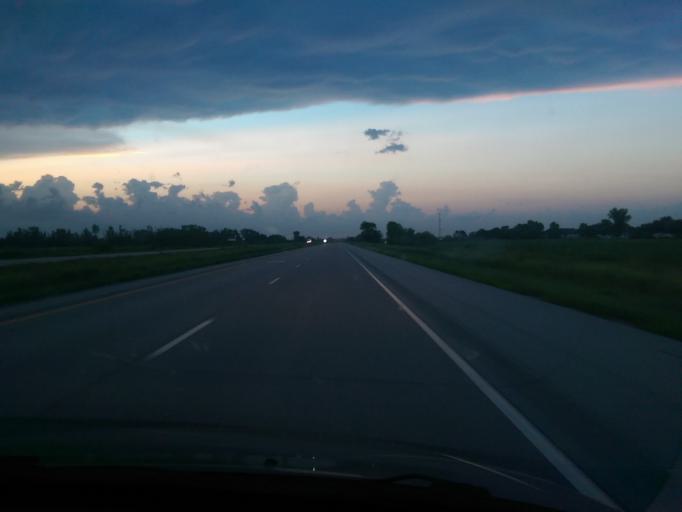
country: US
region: Nebraska
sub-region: Otoe County
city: Nebraska City
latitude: 40.7404
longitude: -95.8174
